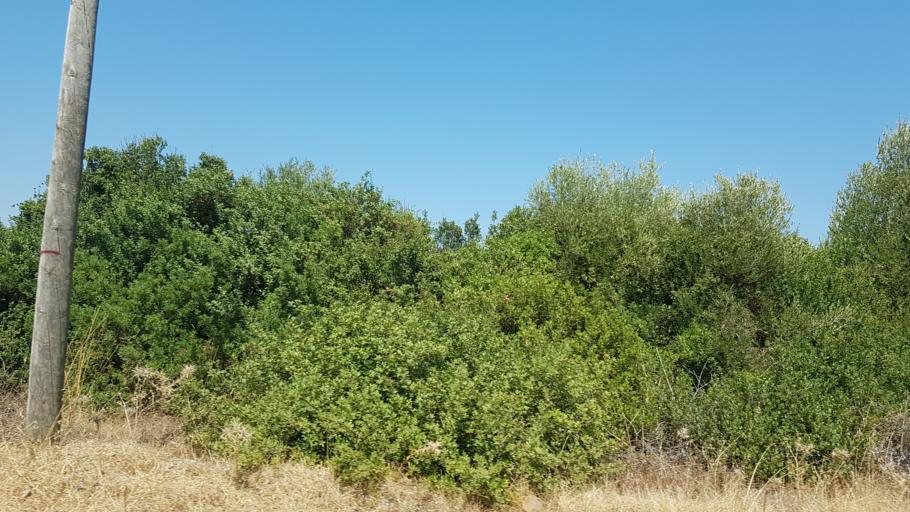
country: TR
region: Mugla
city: Karaova
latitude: 37.1009
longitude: 27.6534
